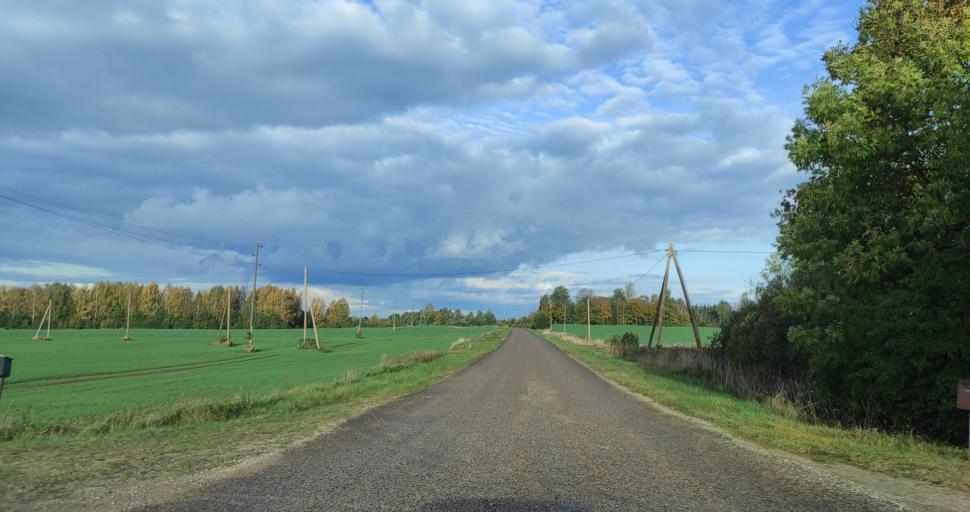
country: LV
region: Aizpute
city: Aizpute
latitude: 56.7780
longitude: 21.7779
